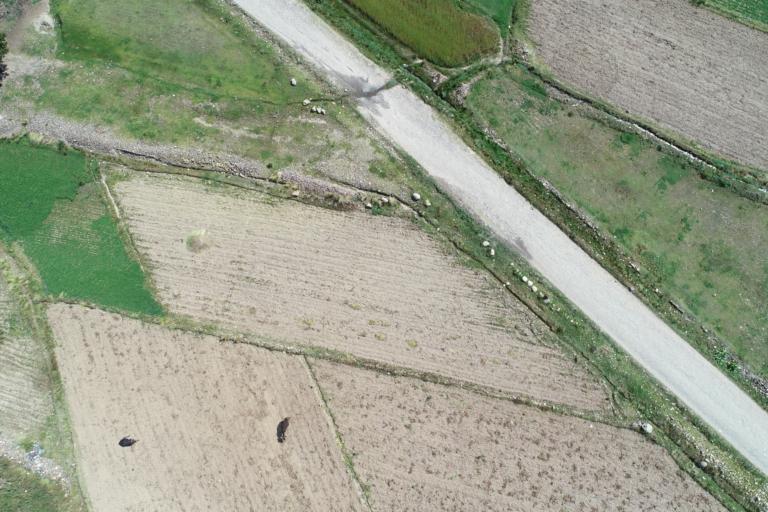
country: BO
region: La Paz
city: Achacachi
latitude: -16.0215
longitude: -68.6162
